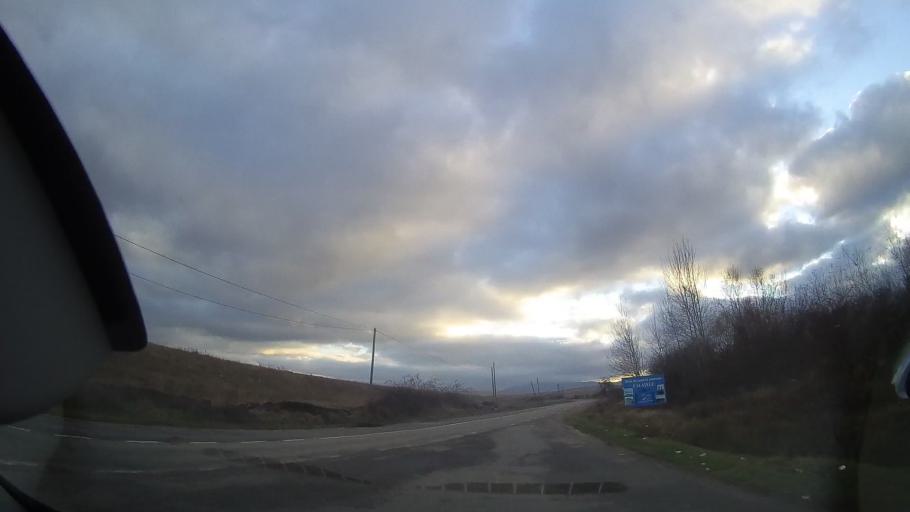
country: RO
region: Cluj
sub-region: Comuna Sancraiu
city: Sancraiu
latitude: 46.8182
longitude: 22.9952
